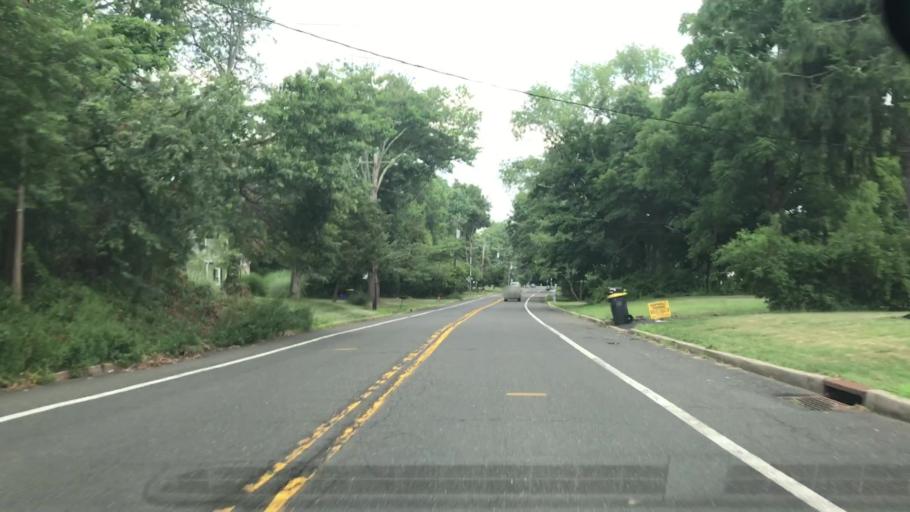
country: US
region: New Jersey
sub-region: Somerset County
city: Bradley Gardens
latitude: 40.5570
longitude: -74.6774
